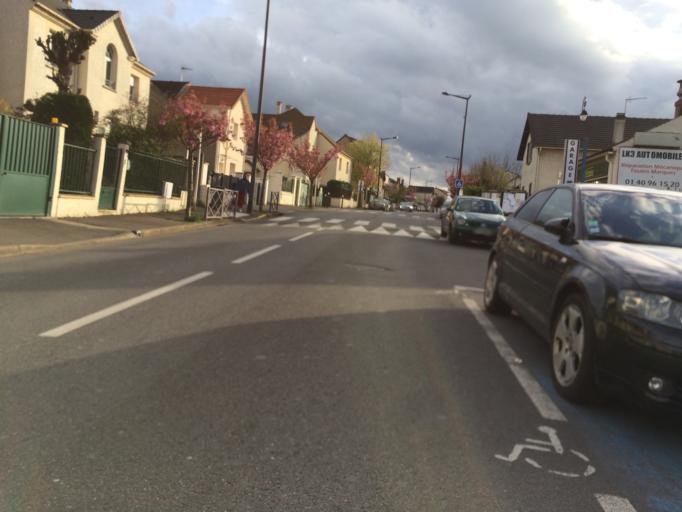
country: FR
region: Ile-de-France
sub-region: Departement des Hauts-de-Seine
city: Antony
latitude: 48.7440
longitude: 2.3120
